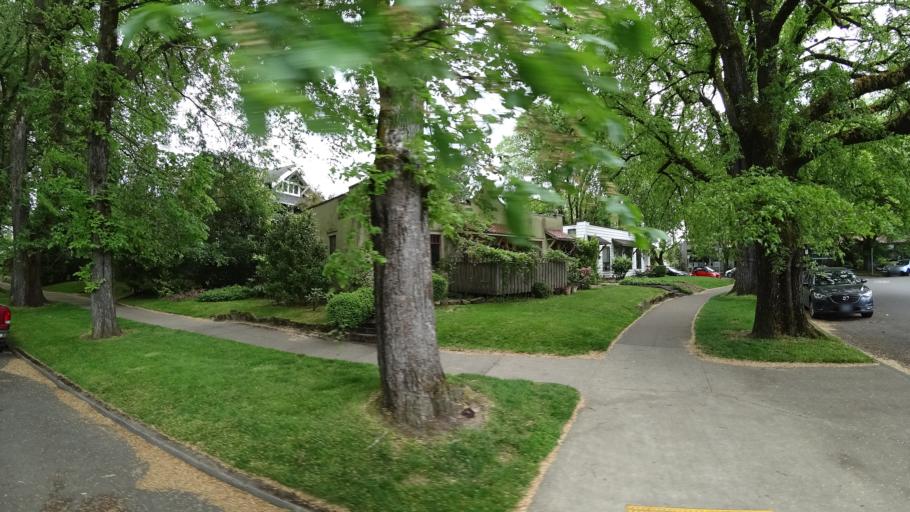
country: US
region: Oregon
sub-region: Multnomah County
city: Portland
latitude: 45.5089
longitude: -122.6489
